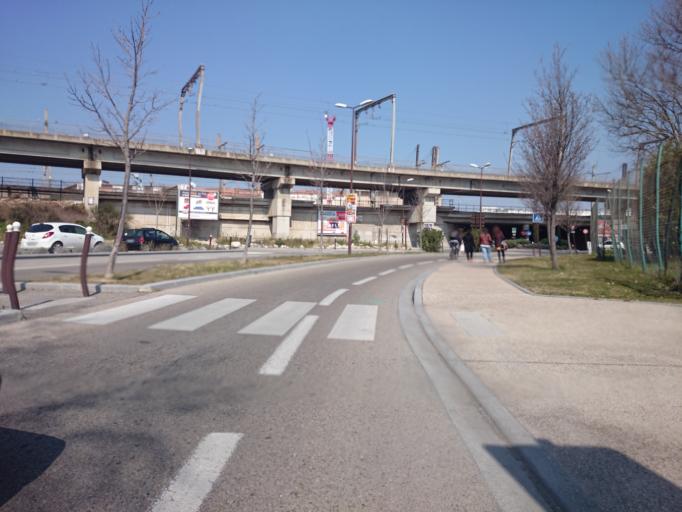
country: FR
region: Provence-Alpes-Cote d'Azur
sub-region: Departement du Vaucluse
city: Avignon
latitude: 43.9406
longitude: 4.7981
